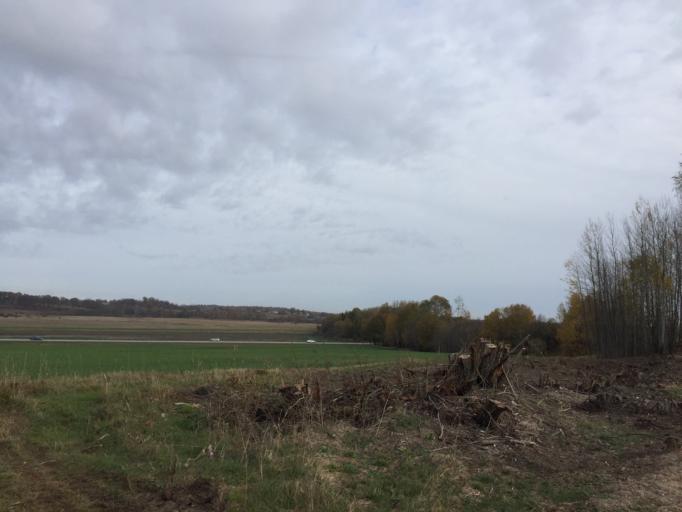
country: LV
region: Tukuma Rajons
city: Tukums
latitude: 56.9557
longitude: 23.0771
